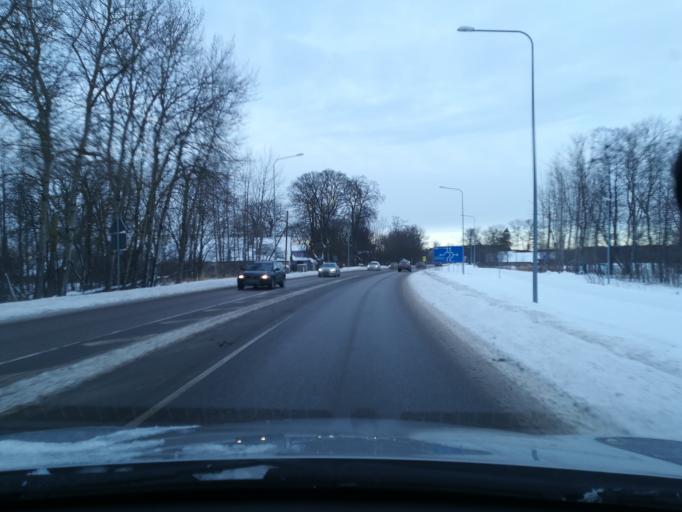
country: EE
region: Harju
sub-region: Harku vald
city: Tabasalu
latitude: 59.4350
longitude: 24.5656
